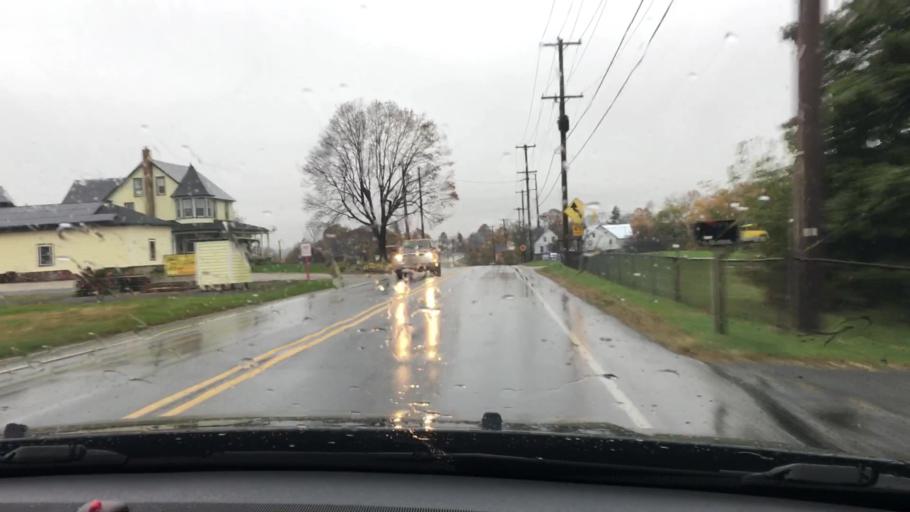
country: US
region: Pennsylvania
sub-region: York County
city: Susquehanna Trails
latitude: 39.8169
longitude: -76.3849
